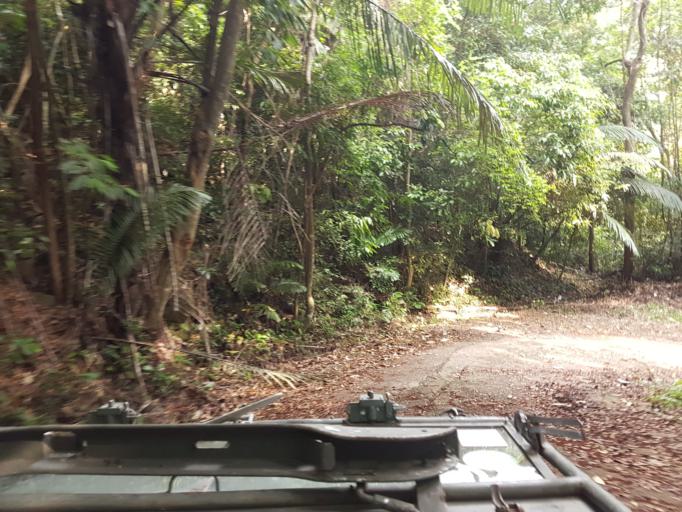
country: TH
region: Pattani
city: Khok Pho
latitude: 6.6575
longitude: 101.0988
